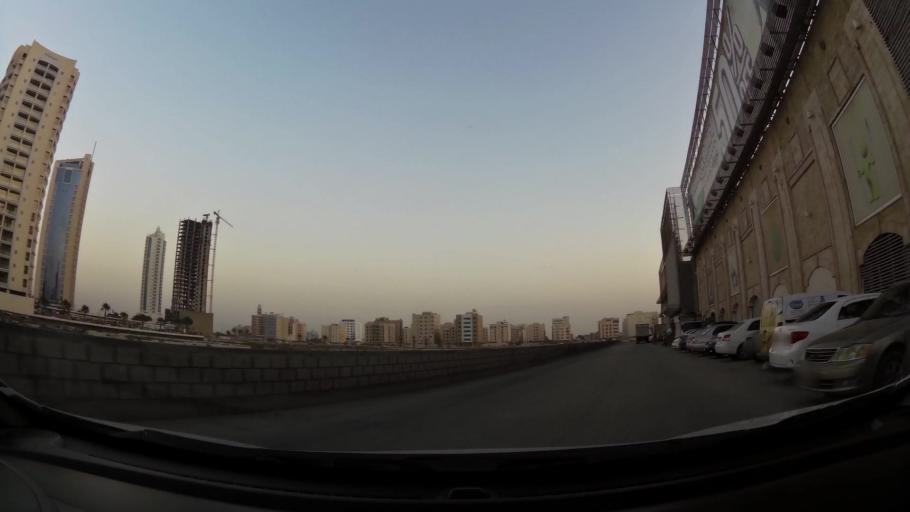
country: BH
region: Manama
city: Jidd Hafs
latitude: 26.2309
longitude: 50.5536
